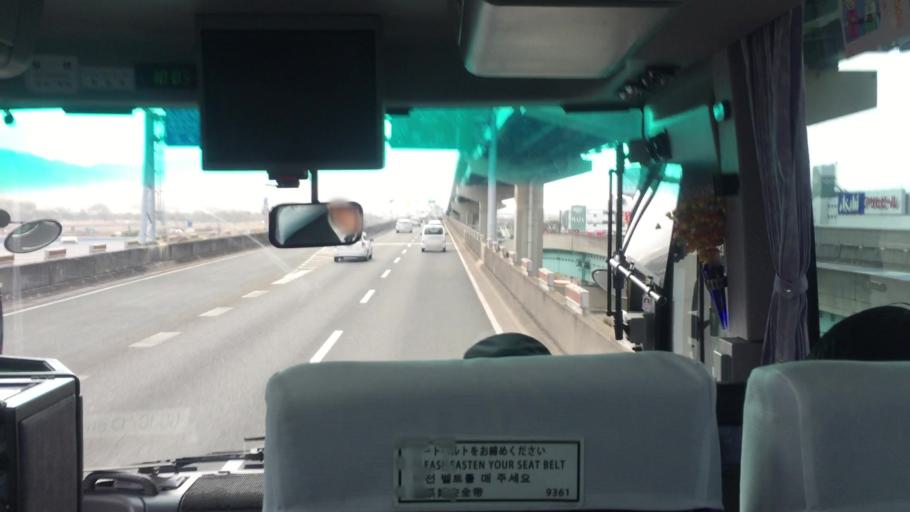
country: JP
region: Fukuoka
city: Onojo
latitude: 33.5737
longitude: 130.4532
